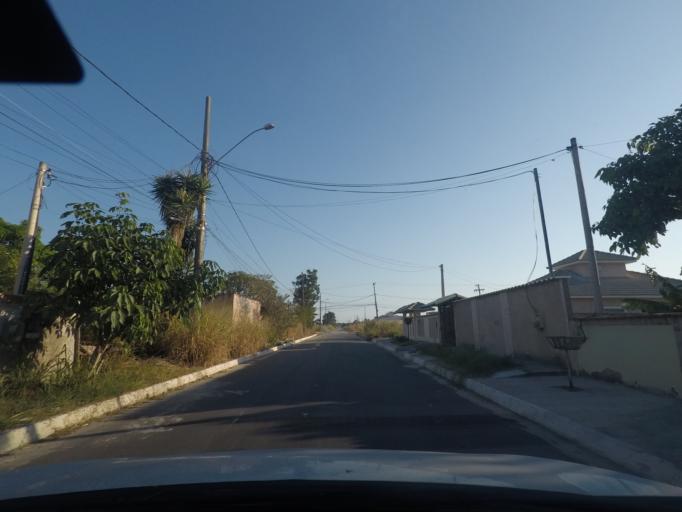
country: BR
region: Rio de Janeiro
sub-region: Marica
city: Marica
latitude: -22.9587
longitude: -42.9326
